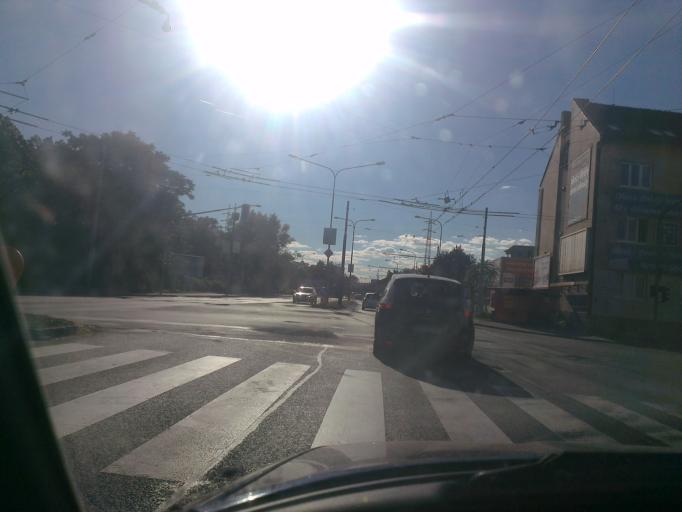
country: CZ
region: South Moravian
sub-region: Mesto Brno
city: Brno
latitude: 49.1900
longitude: 16.6315
